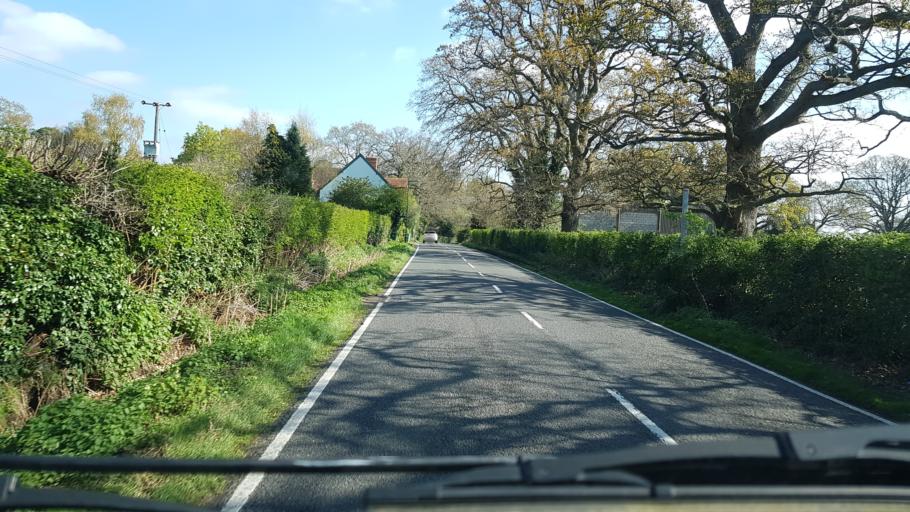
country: GB
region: England
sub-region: Surrey
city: Knaphill
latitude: 51.2908
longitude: -0.6118
